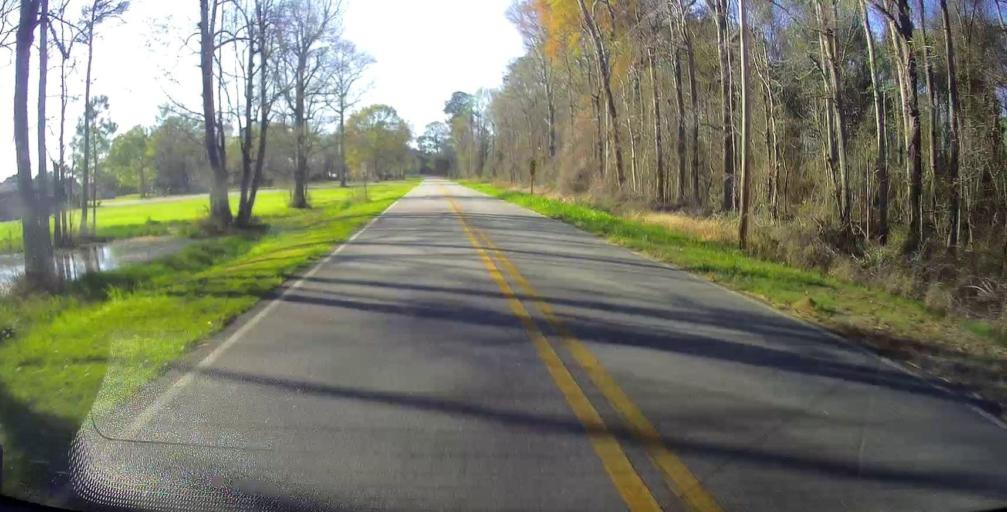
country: US
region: Georgia
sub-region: Houston County
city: Perry
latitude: 32.3620
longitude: -83.6539
